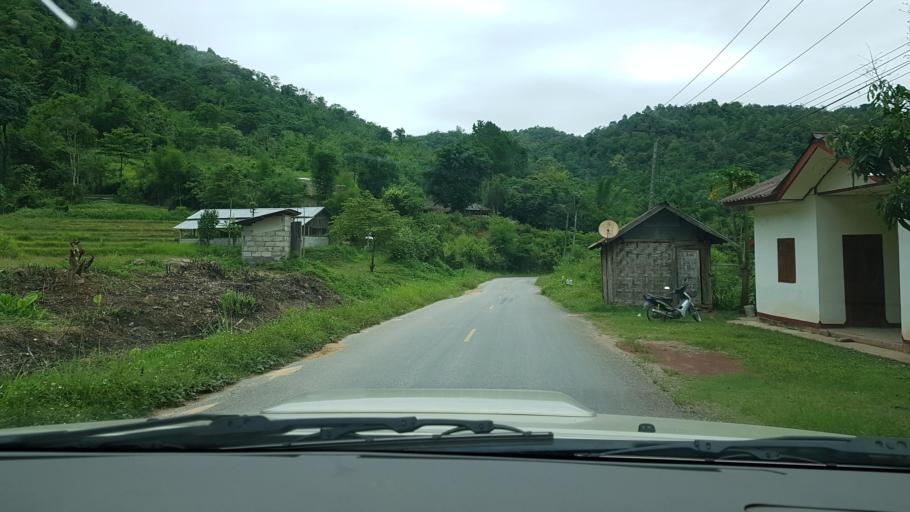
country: LA
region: Oudomxai
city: Muang La
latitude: 20.7870
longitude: 102.0716
